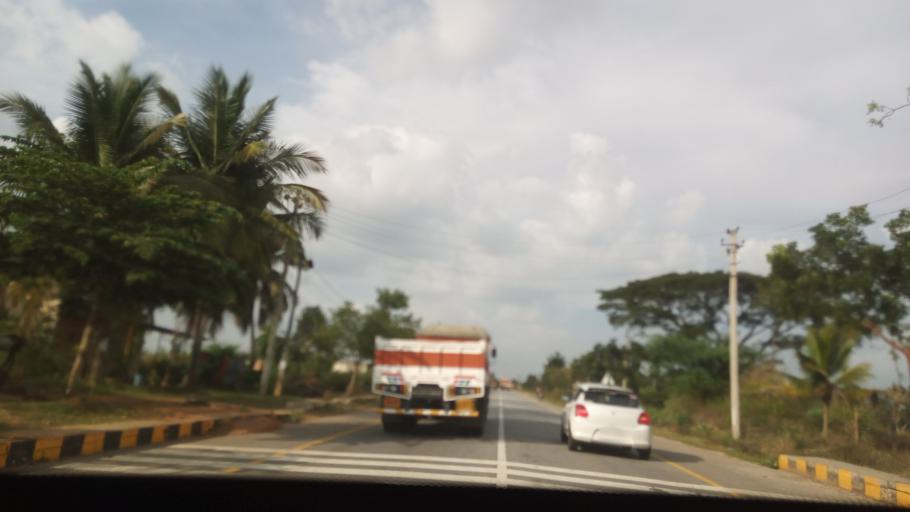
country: IN
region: Karnataka
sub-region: Tumkur
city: Kunigal
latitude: 12.8673
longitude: 77.0404
